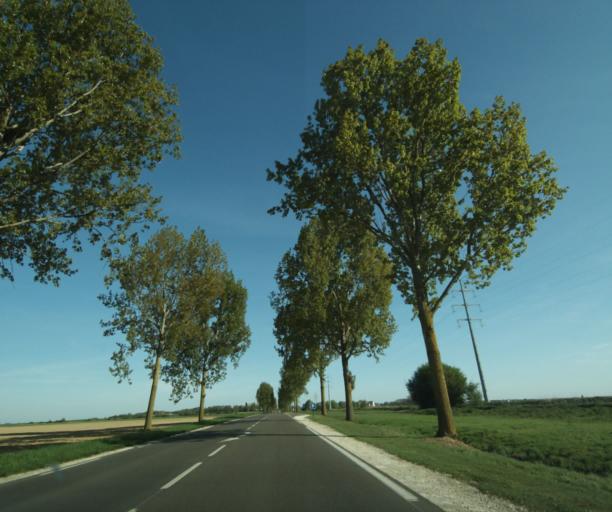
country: FR
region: Ile-de-France
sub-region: Departement de Seine-et-Marne
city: Bailly-Carrois
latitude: 48.5740
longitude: 2.9961
